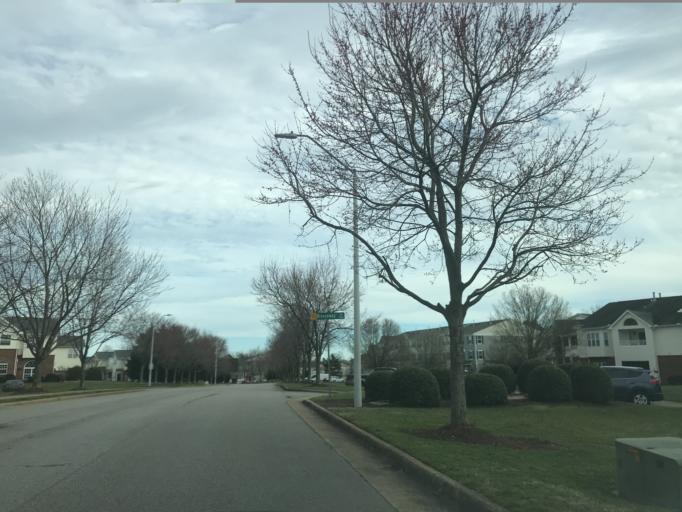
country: US
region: North Carolina
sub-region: Wake County
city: Wake Forest
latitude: 35.9240
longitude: -78.5708
